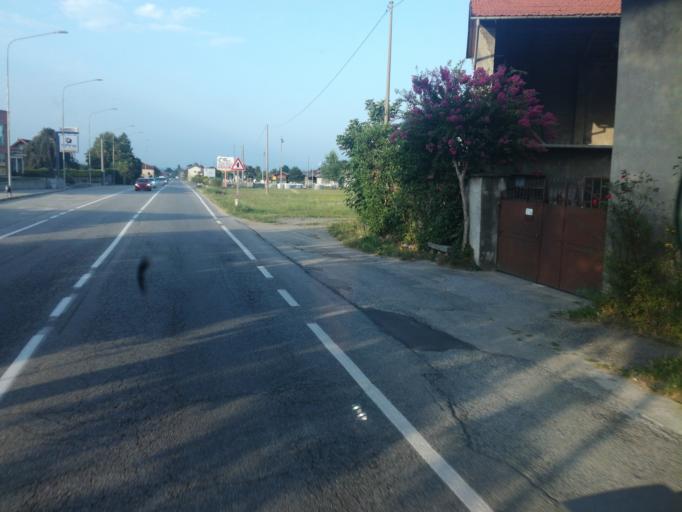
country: IT
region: Piedmont
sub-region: Provincia di Torino
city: Bibiana
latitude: 44.8099
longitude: 7.2911
